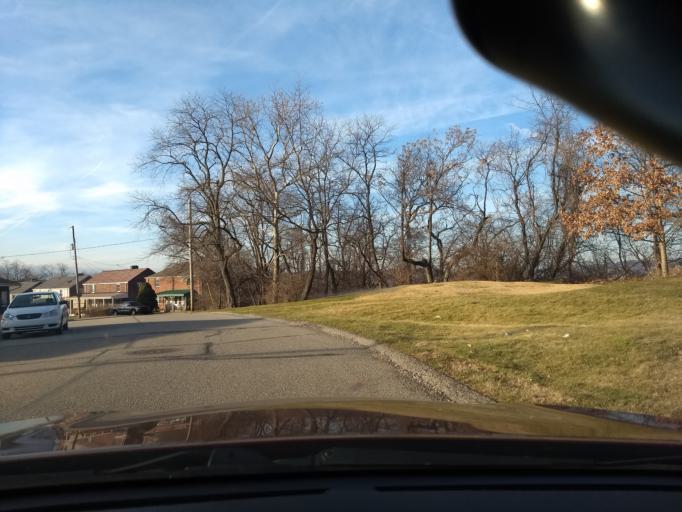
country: US
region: Pennsylvania
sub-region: Allegheny County
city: Whitaker
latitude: 40.4037
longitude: -79.8861
